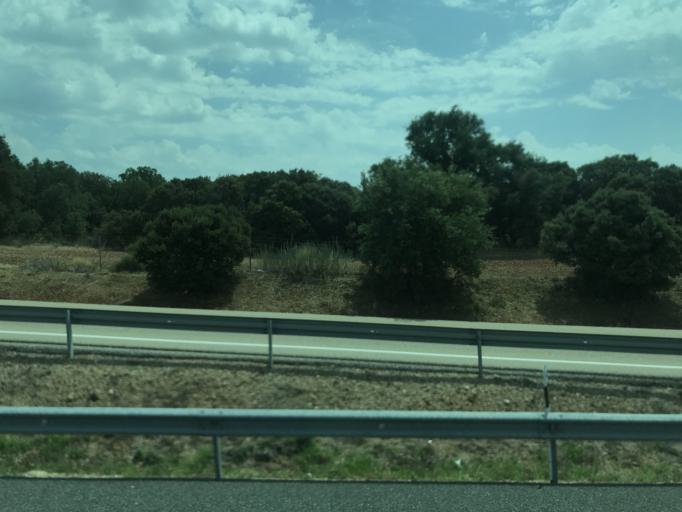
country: ES
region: Castille and Leon
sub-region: Provincia de Burgos
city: Madrigalejo del Monte
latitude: 42.0905
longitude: -3.7277
